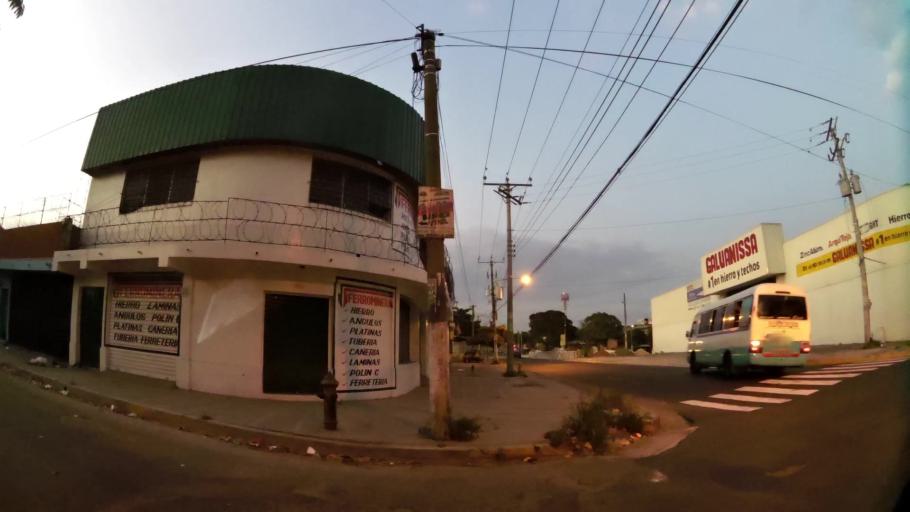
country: SV
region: San Salvador
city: San Salvador
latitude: 13.7070
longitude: -89.1894
